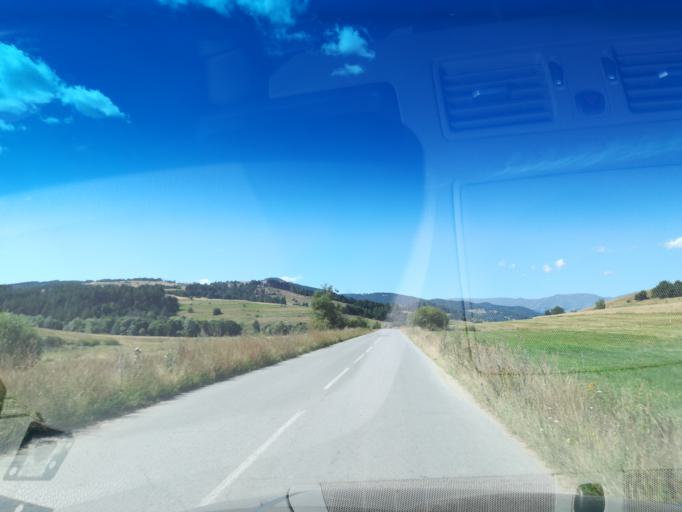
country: BG
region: Sofiya
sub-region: Obshtina Koprivshtitsa
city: Koprivshtitsa
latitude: 42.6047
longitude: 24.3796
